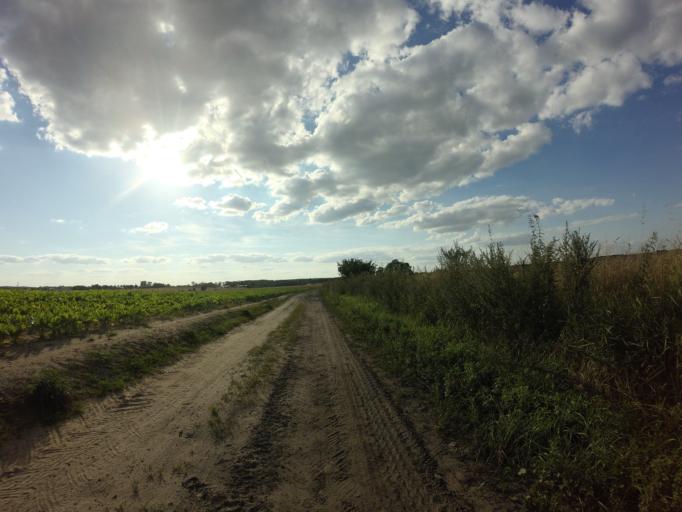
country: PL
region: West Pomeranian Voivodeship
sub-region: Powiat choszczenski
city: Choszczno
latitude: 53.2035
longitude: 15.4064
